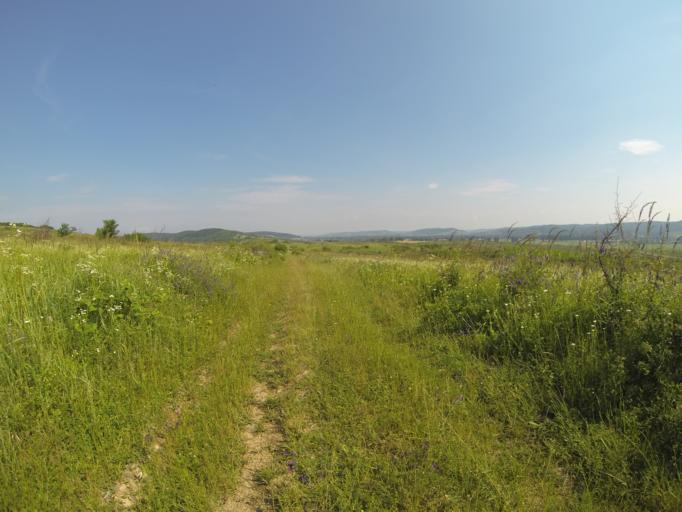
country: RO
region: Gorj
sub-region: Comuna Crusetu
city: Crusetu
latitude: 44.6095
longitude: 23.6693
